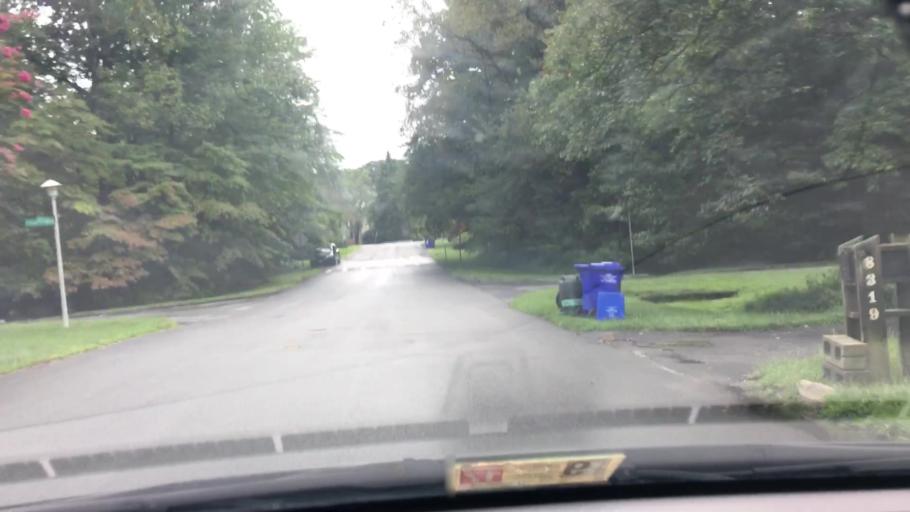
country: US
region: Maryland
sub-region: Montgomery County
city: Cabin John
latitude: 38.9862
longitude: -77.1718
